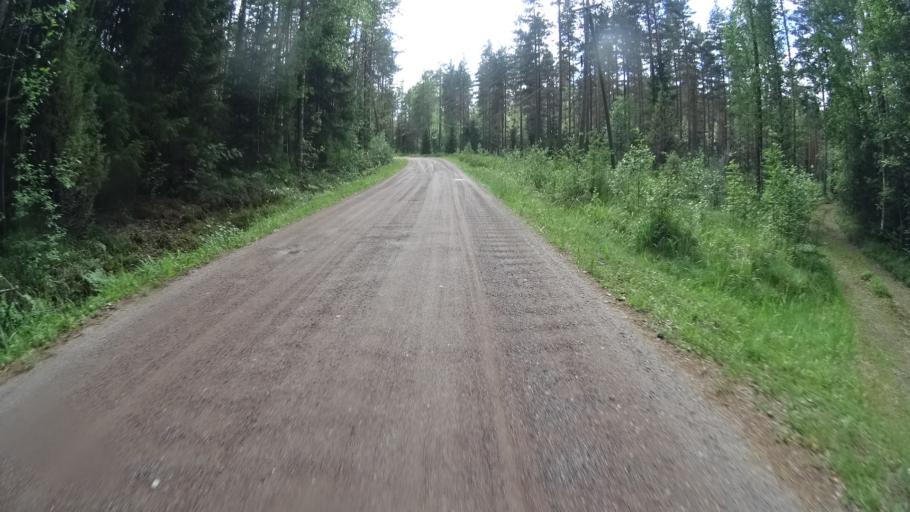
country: FI
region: Uusimaa
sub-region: Helsinki
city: Karkkila
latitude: 60.6036
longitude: 24.1820
